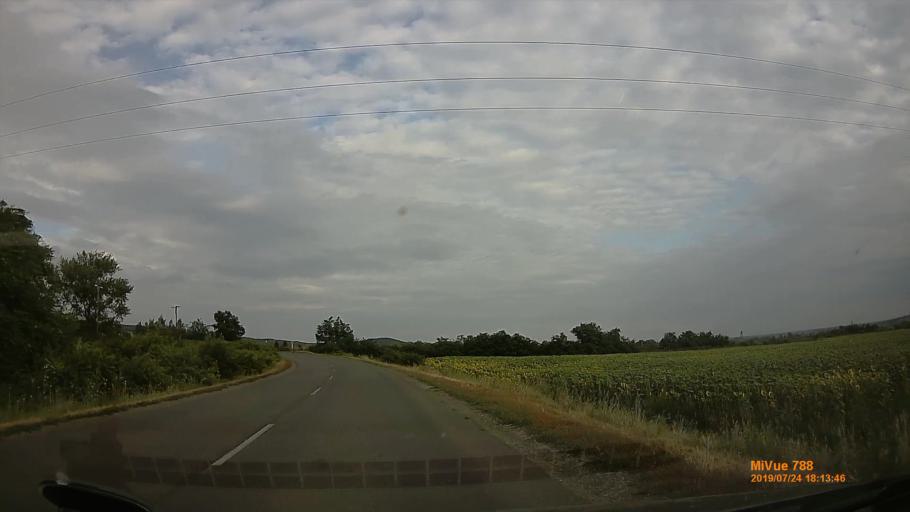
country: HU
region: Borsod-Abauj-Zemplen
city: Tallya
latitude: 48.2260
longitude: 21.2225
